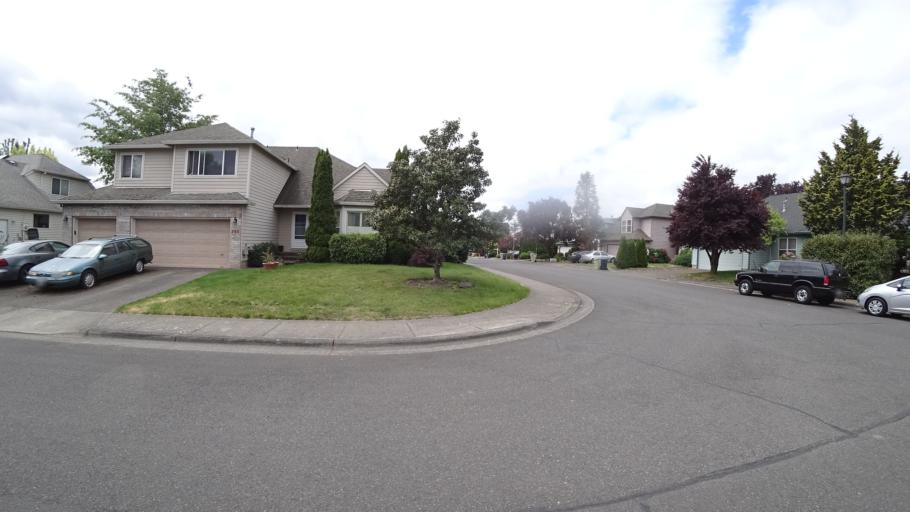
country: US
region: Oregon
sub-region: Washington County
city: Oak Hills
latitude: 45.5238
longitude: -122.8625
